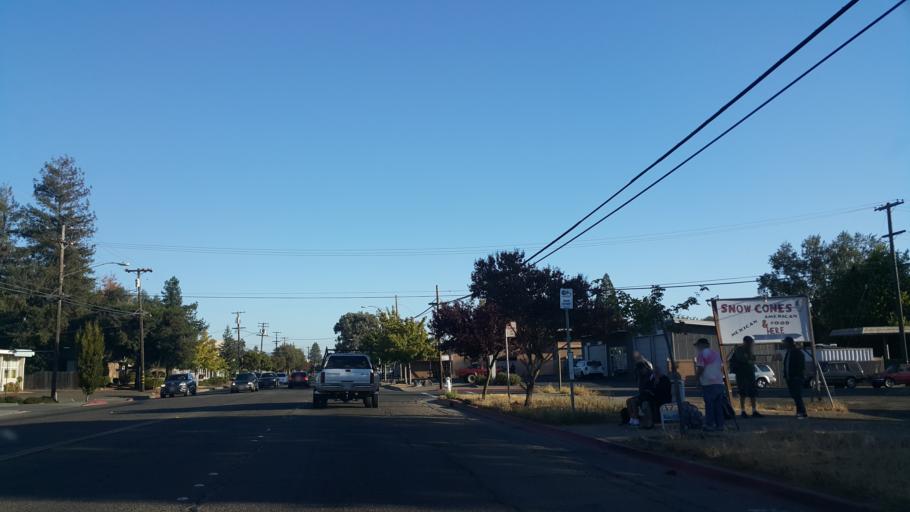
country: US
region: California
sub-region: Mendocino County
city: Ukiah
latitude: 39.1391
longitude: -123.2058
